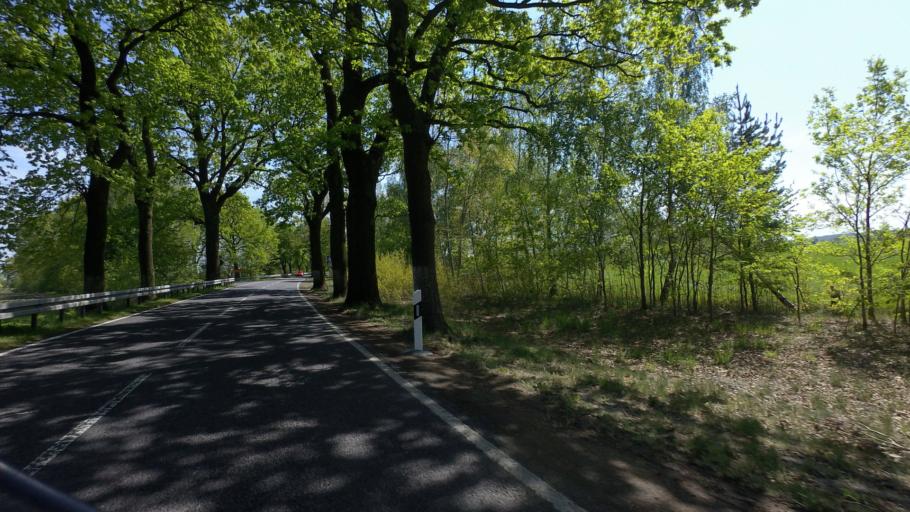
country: DE
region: Brandenburg
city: Munchehofe
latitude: 52.0947
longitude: 13.8453
